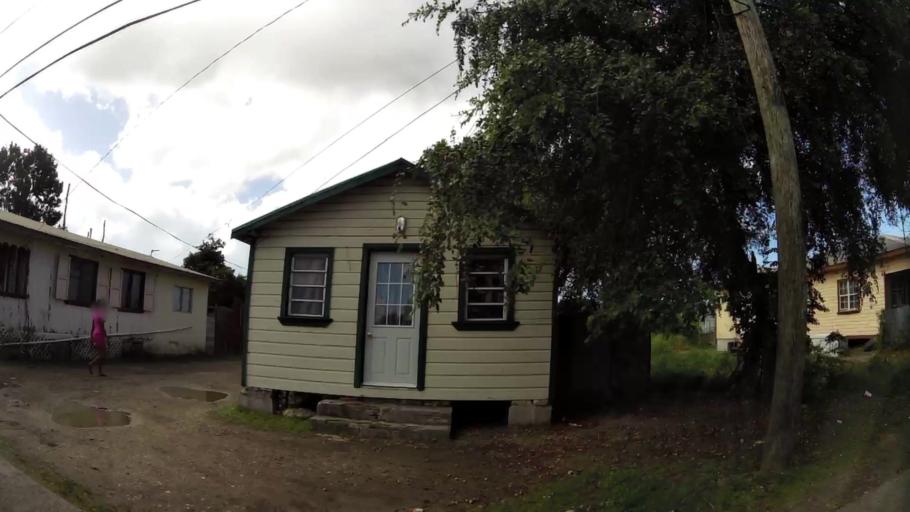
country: AG
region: Saint John
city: Saint John's
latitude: 17.1126
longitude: -61.8446
